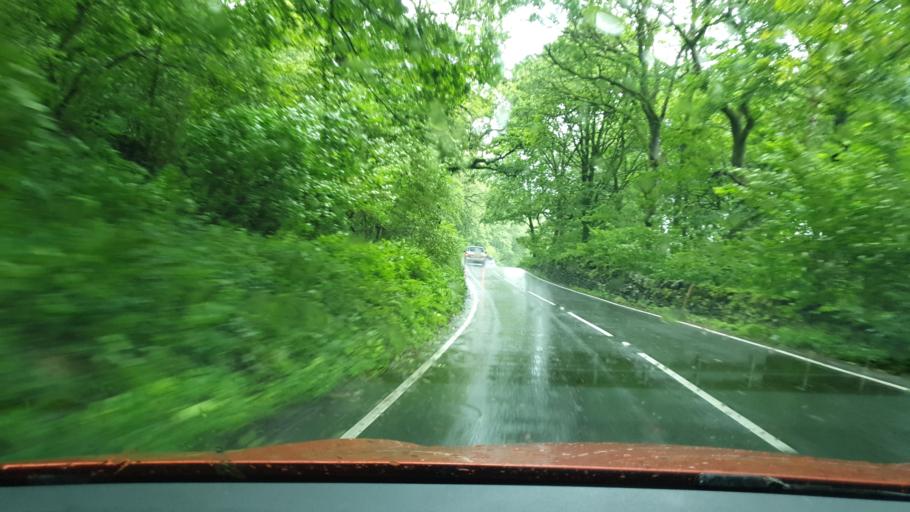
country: GB
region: England
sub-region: Cumbria
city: Ambleside
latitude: 54.3500
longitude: -3.0867
